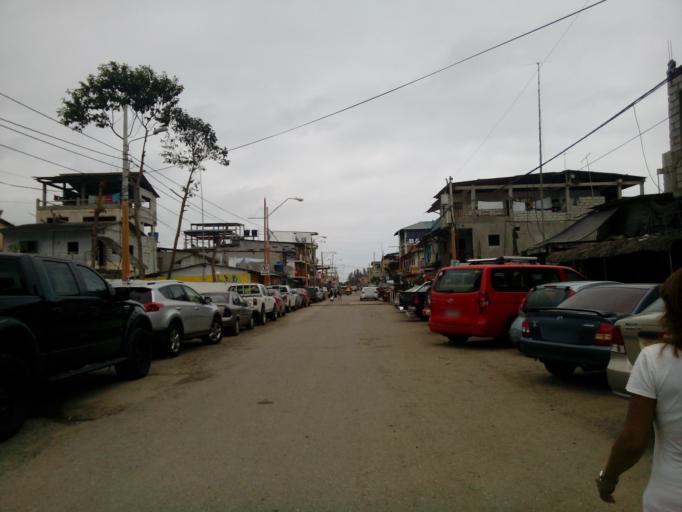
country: EC
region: Santa Elena
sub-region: Canton Santa Elena
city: Santa Elena
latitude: -1.8275
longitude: -80.7524
